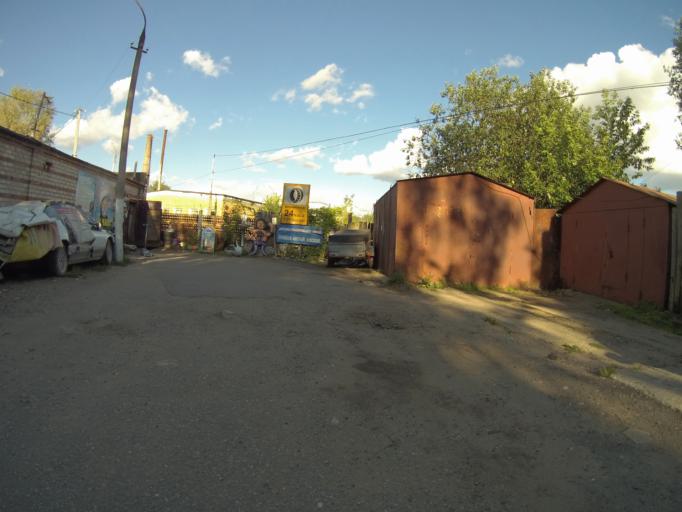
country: RU
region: Vladimir
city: Vladimir
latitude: 56.1238
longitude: 40.3672
